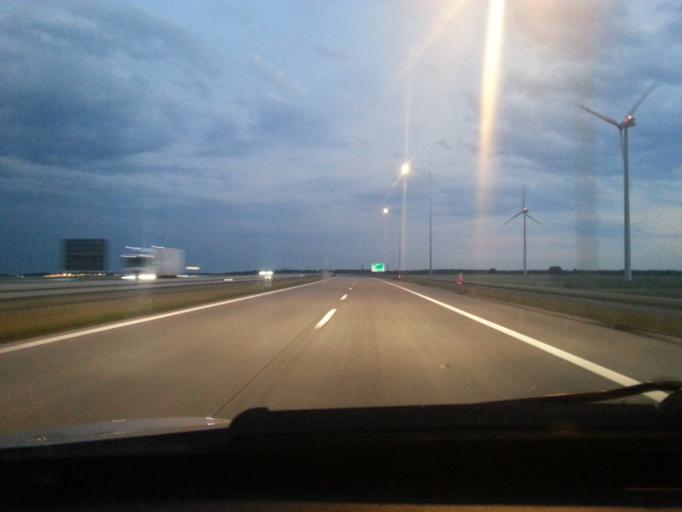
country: PL
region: Lodz Voivodeship
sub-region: Powiat sieradzki
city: Sieradz
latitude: 51.5535
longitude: 18.7111
